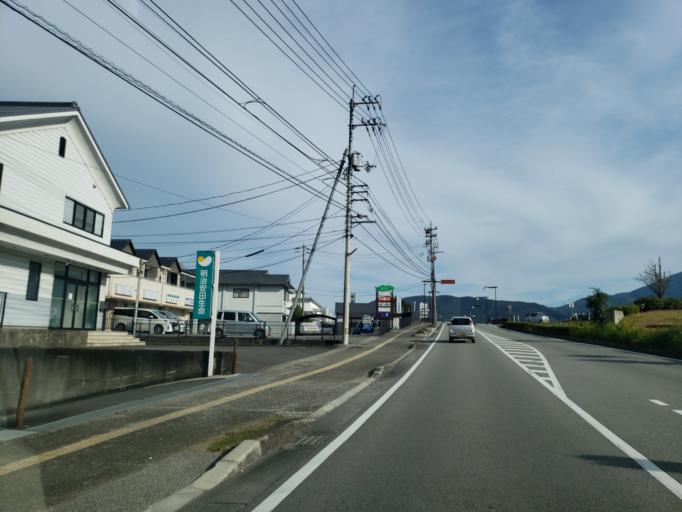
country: JP
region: Tokushima
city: Wakimachi
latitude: 34.0665
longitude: 134.1472
